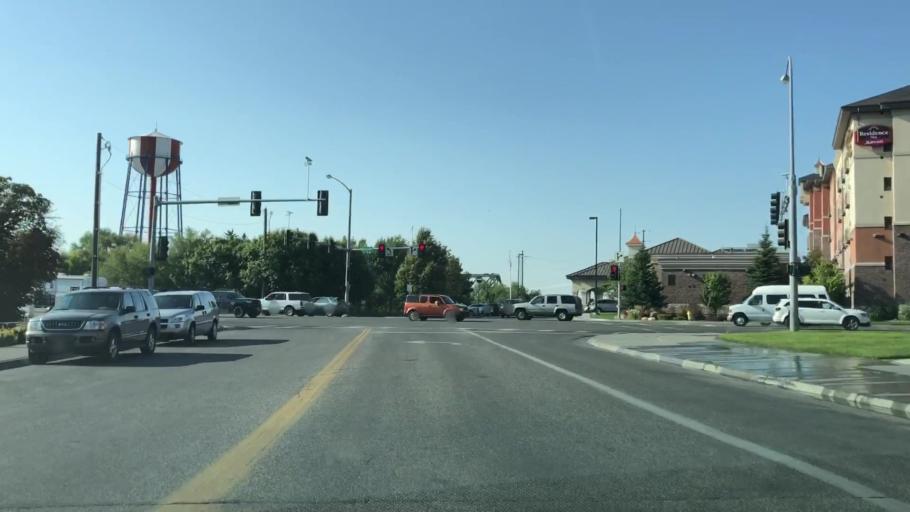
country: US
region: Idaho
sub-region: Bonneville County
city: Idaho Falls
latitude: 43.4938
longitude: -112.0452
